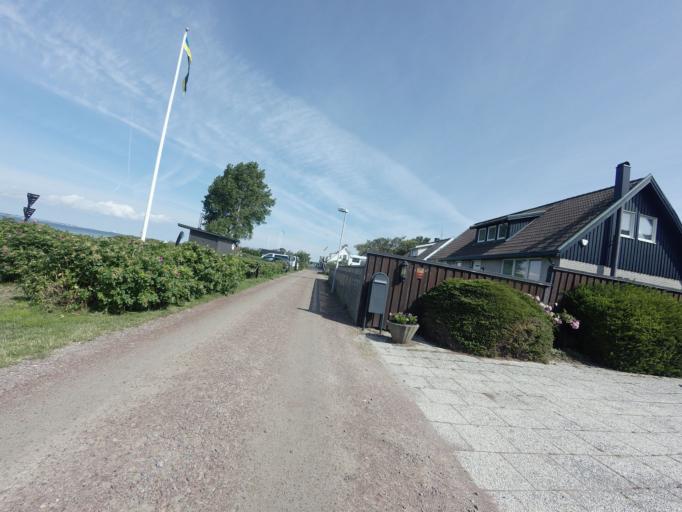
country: SE
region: Skane
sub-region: Helsingborg
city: Rydeback
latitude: 55.9572
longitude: 12.7586
